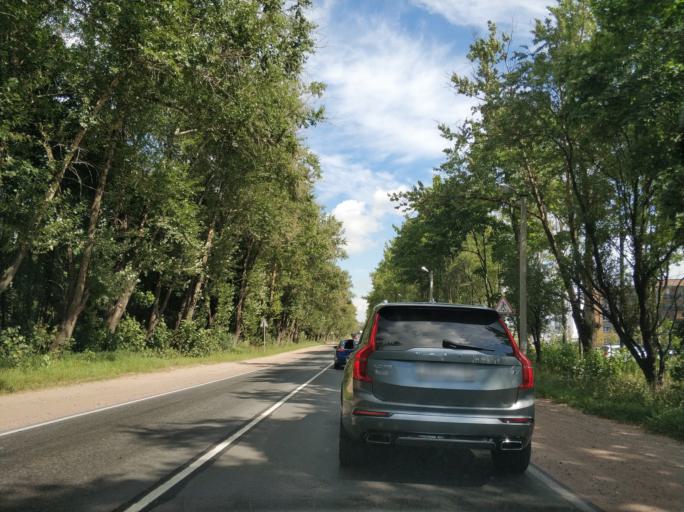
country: RU
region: Leningrad
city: Vsevolozhsk
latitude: 60.0373
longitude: 30.6515
